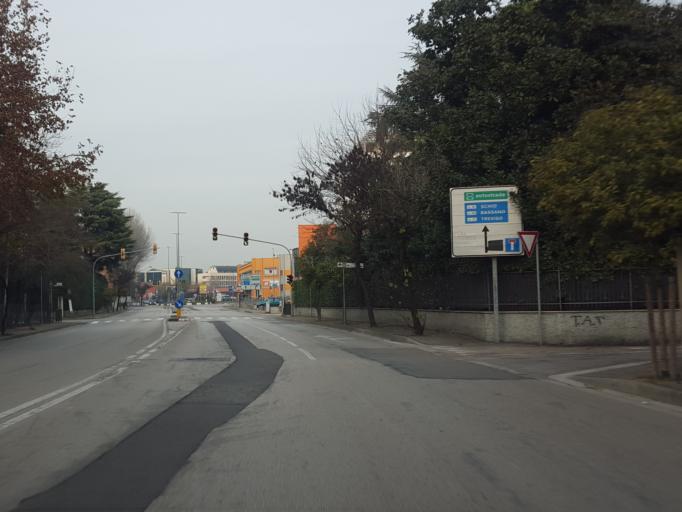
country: IT
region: Veneto
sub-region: Provincia di Vicenza
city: Vicenza
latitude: 45.5518
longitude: 11.5641
